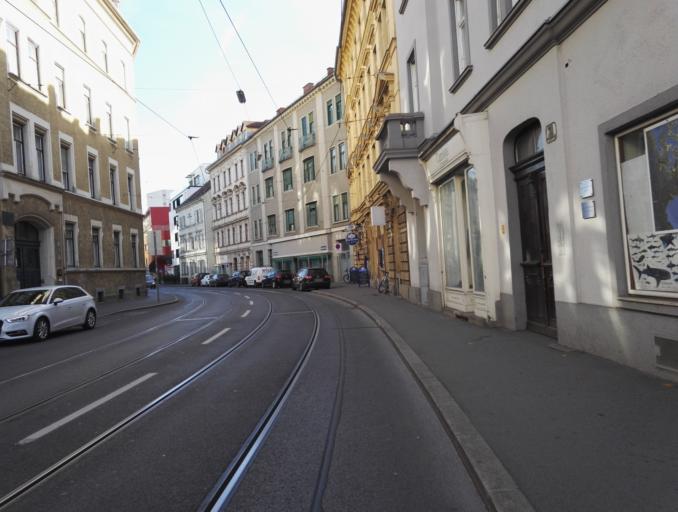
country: AT
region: Styria
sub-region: Graz Stadt
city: Graz
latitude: 47.0646
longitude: 15.4484
